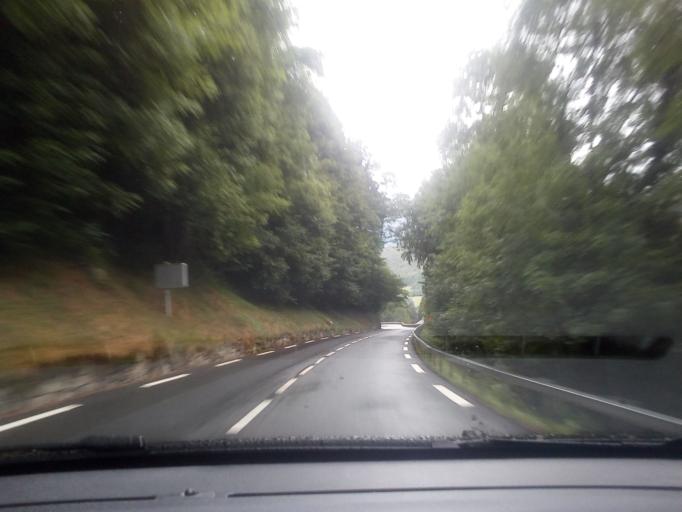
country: FR
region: Midi-Pyrenees
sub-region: Departement des Hautes-Pyrenees
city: Campan
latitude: 42.9431
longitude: 0.2178
